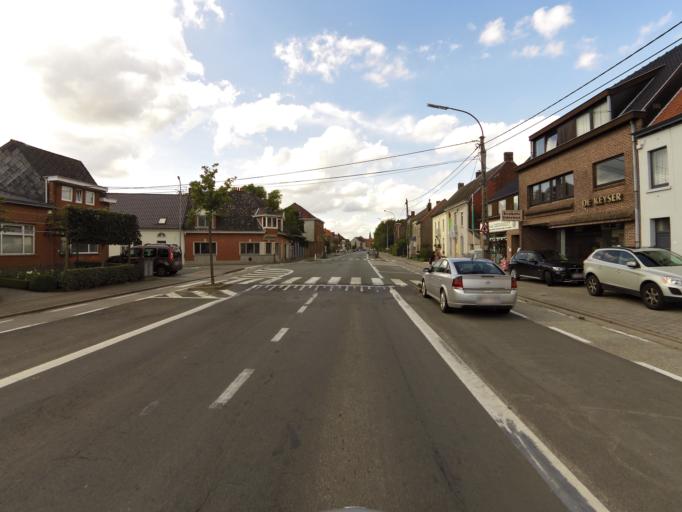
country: BE
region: Flanders
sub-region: Provincie West-Vlaanderen
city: Anzegem
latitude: 50.7851
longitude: 3.5139
